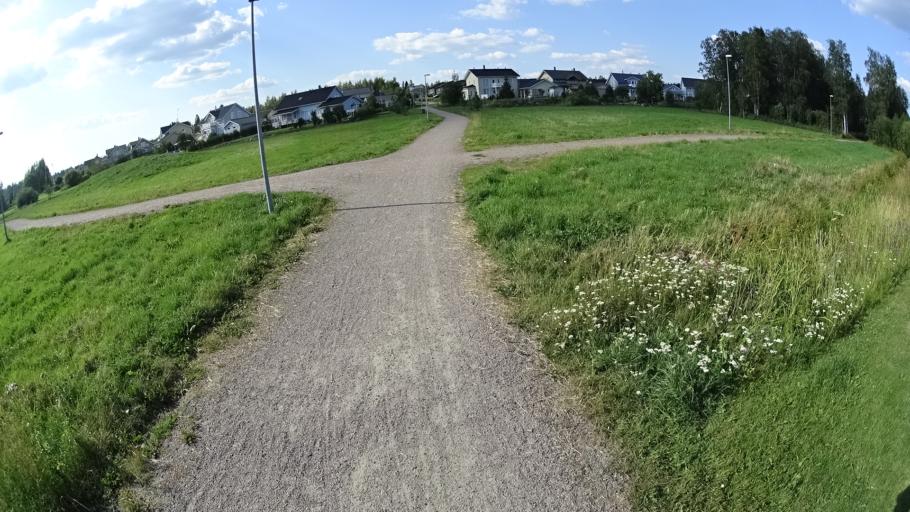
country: FI
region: Uusimaa
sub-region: Porvoo
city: Porvoo
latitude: 60.4119
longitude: 25.6611
